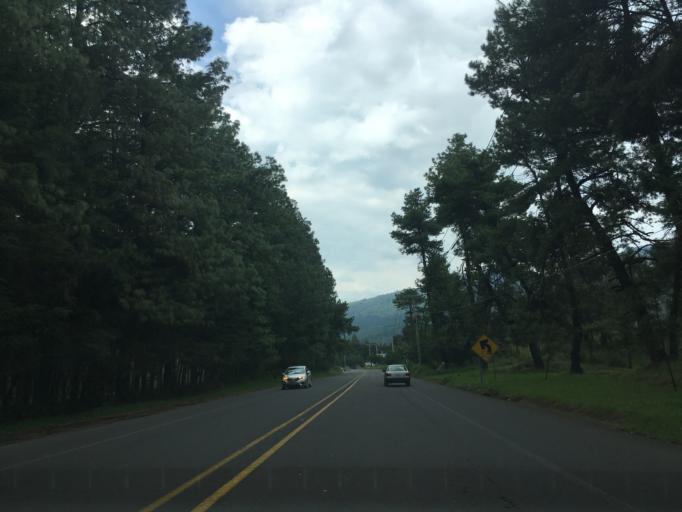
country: MX
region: Michoacan
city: Capacuaro
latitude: 19.5305
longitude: -102.0796
